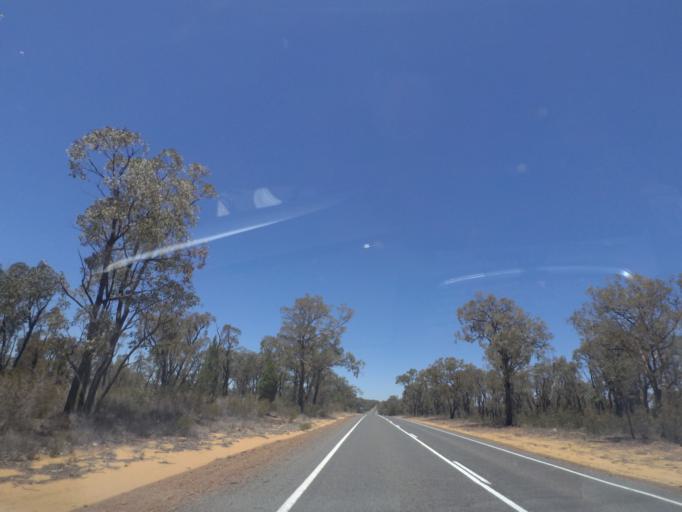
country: AU
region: New South Wales
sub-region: Narrabri
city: Narrabri
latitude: -30.7163
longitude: 149.5276
